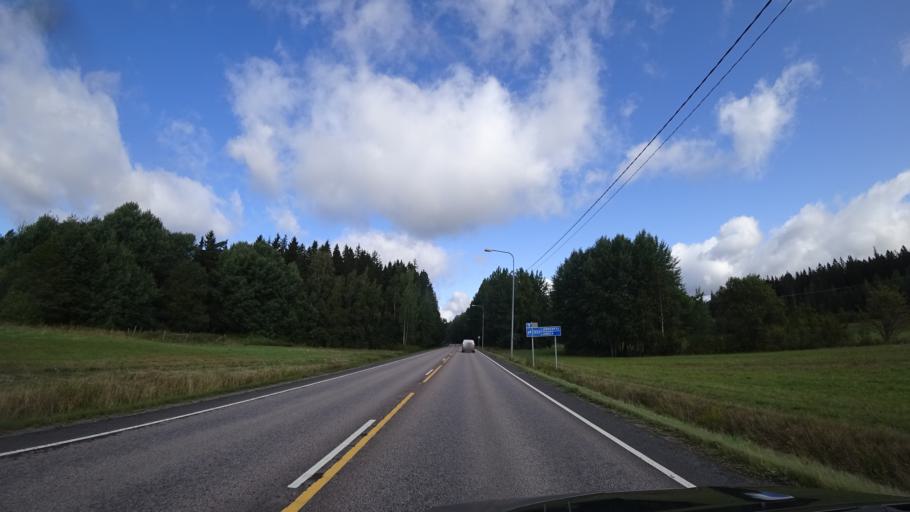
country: FI
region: Uusimaa
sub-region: Helsinki
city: Hyvinge
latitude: 60.5301
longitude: 24.9216
